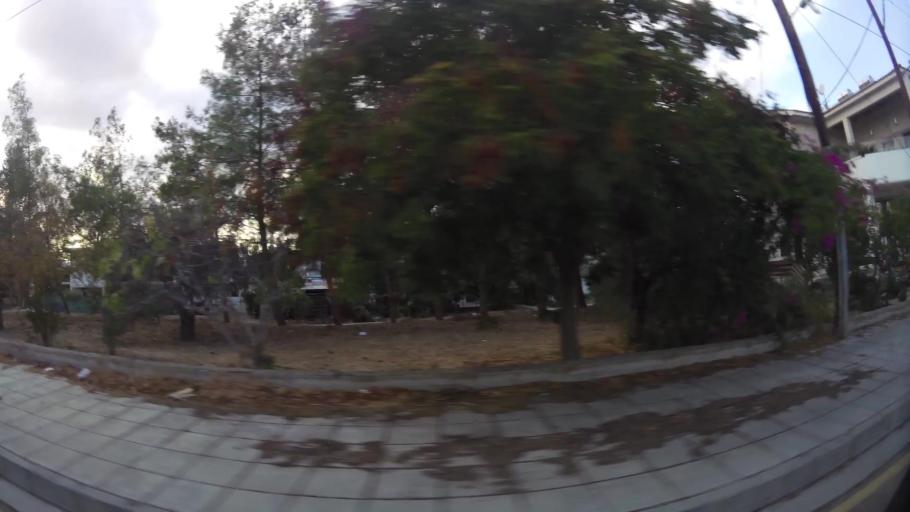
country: CY
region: Lefkosia
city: Kato Deftera
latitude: 35.1124
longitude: 33.3021
